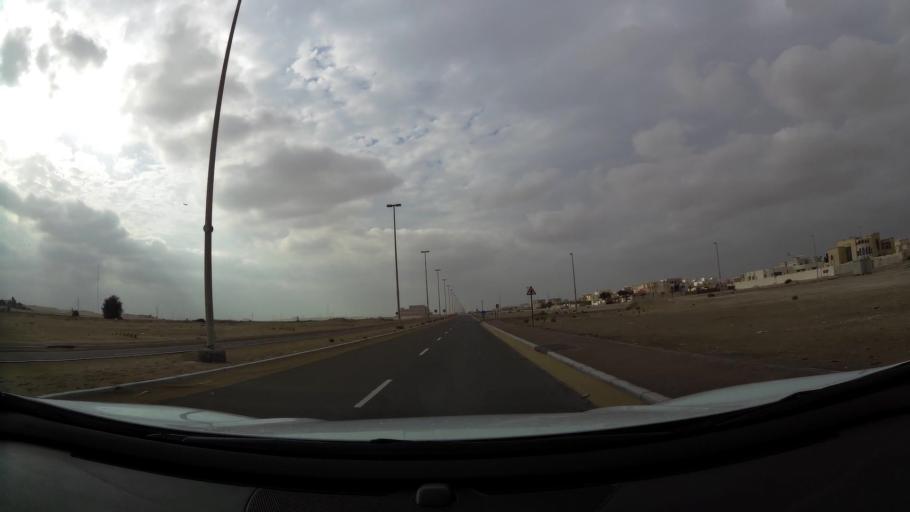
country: AE
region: Abu Dhabi
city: Abu Dhabi
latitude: 24.3372
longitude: 54.6221
